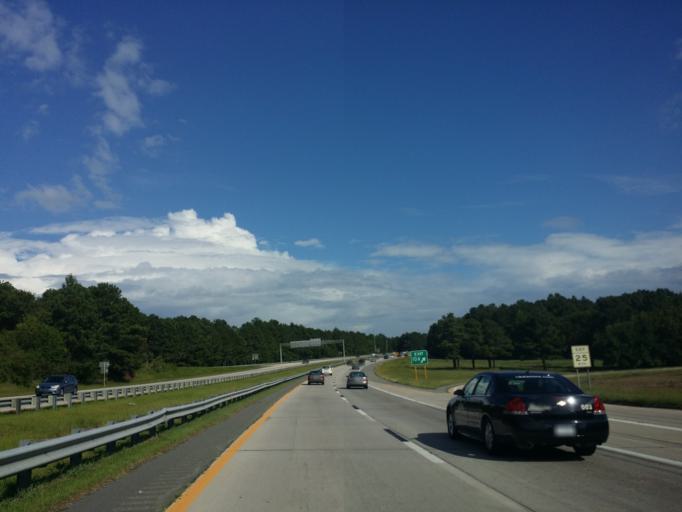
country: US
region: North Carolina
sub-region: Durham County
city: Durham
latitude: 35.9761
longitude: -78.8752
